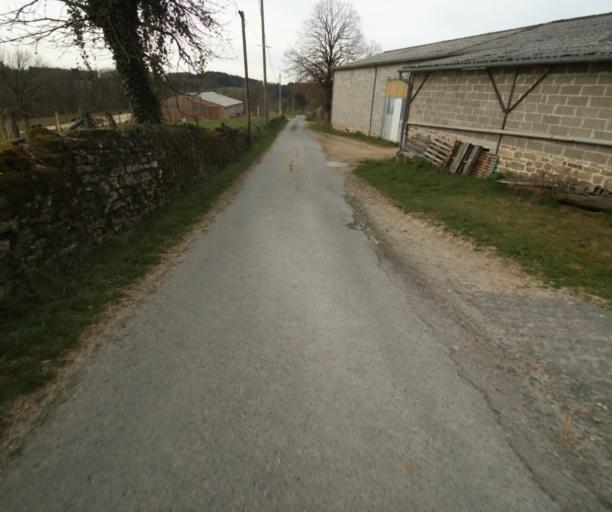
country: FR
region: Limousin
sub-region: Departement de la Correze
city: Correze
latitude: 45.4346
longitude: 1.8249
